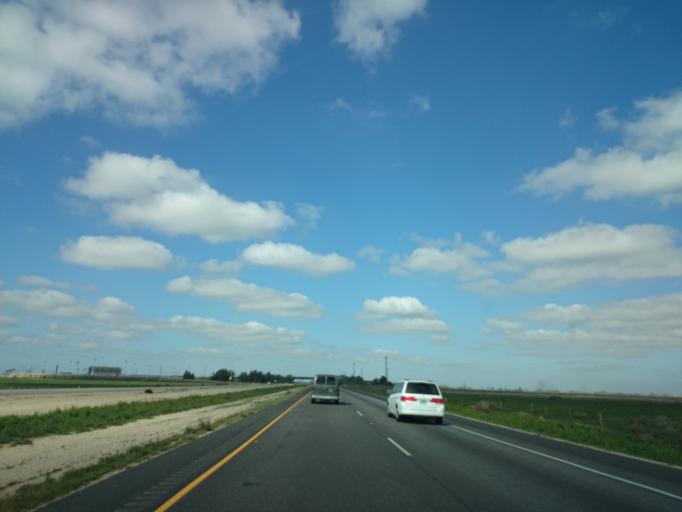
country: US
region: California
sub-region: Kern County
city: Rosedale
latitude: 35.2879
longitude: -119.2465
